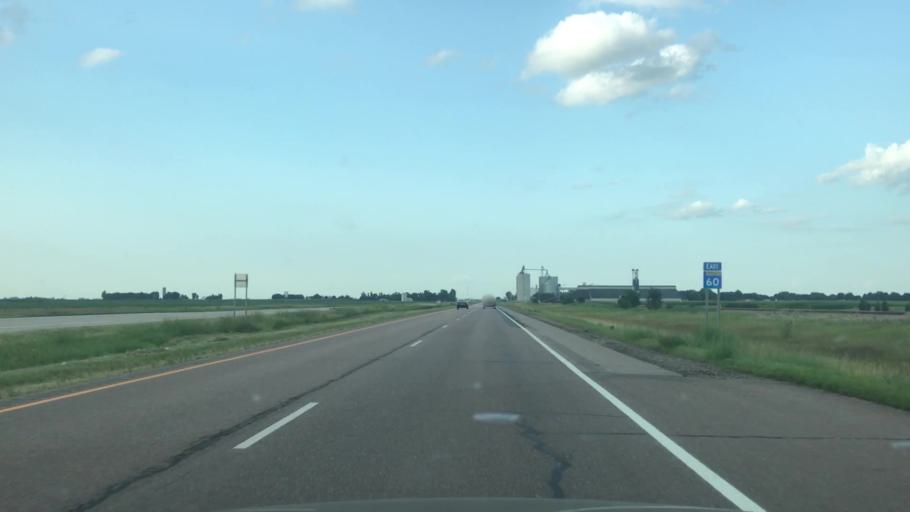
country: US
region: Minnesota
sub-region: Nobles County
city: Worthington
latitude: 43.6887
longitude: -95.4868
